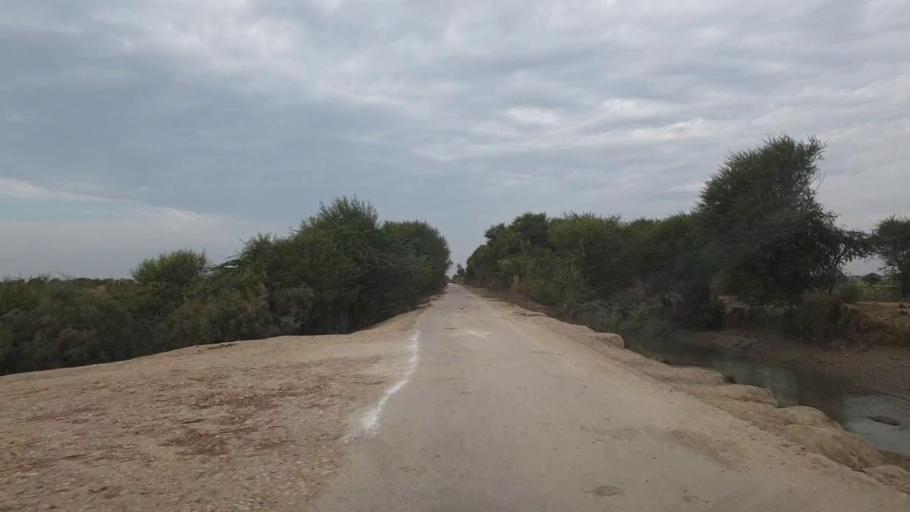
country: PK
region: Sindh
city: Jhol
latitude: 25.9961
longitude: 68.8902
